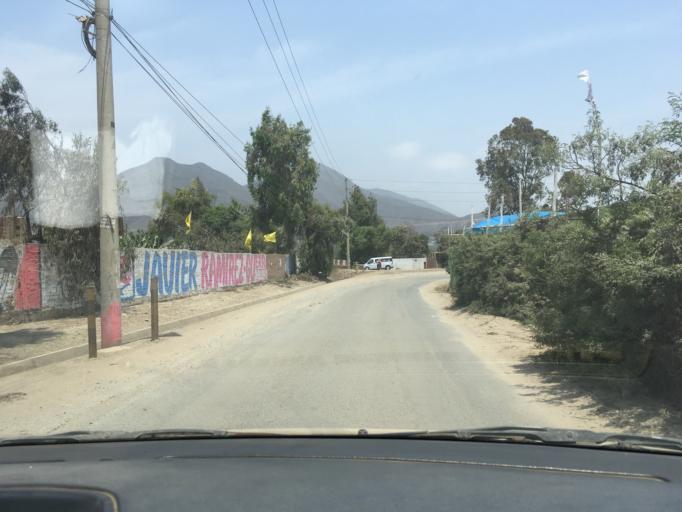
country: PE
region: Lima
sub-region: Lima
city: Cieneguilla
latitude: -12.1741
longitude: -76.8616
